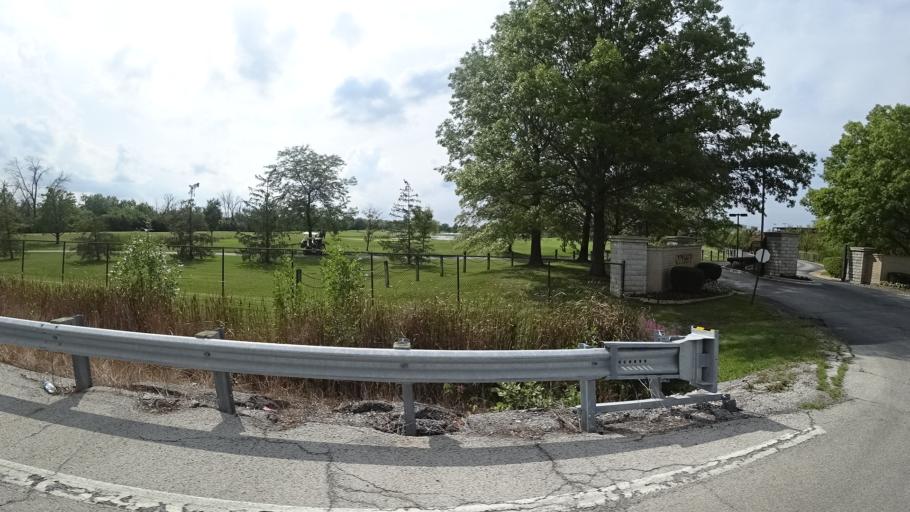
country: US
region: Illinois
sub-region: Cook County
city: Tinley Park
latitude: 41.5400
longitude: -87.7711
